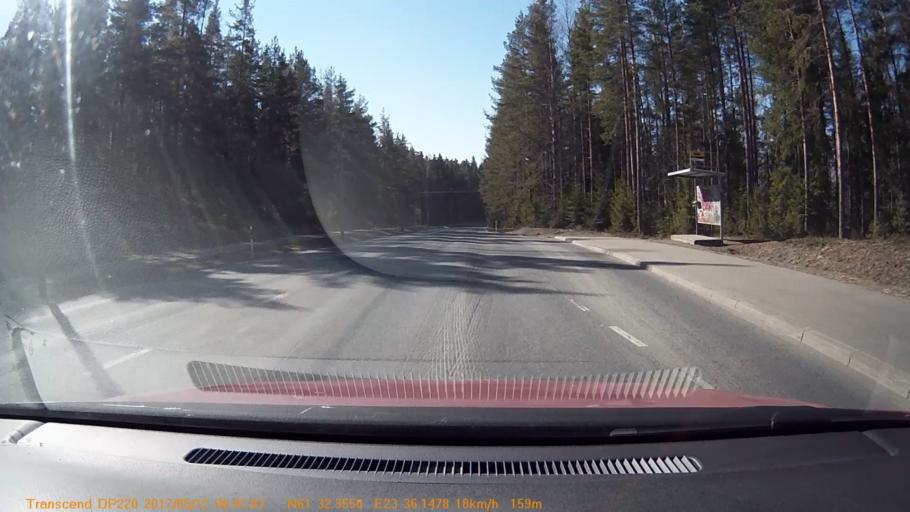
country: FI
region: Pirkanmaa
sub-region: Tampere
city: Yloejaervi
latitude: 61.5393
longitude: 23.6024
